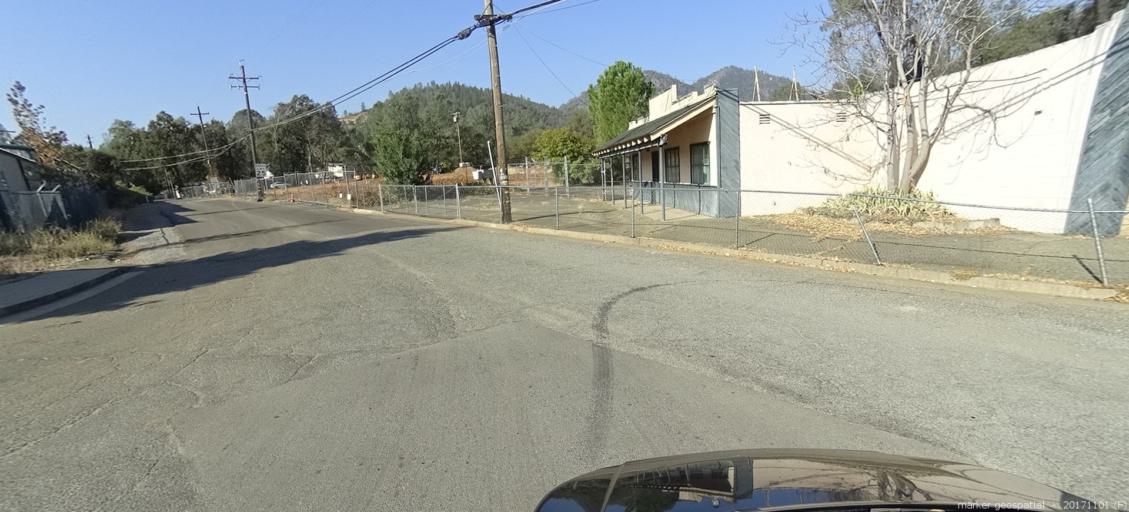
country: US
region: California
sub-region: Shasta County
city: Shasta Lake
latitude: 40.7165
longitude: -122.3312
